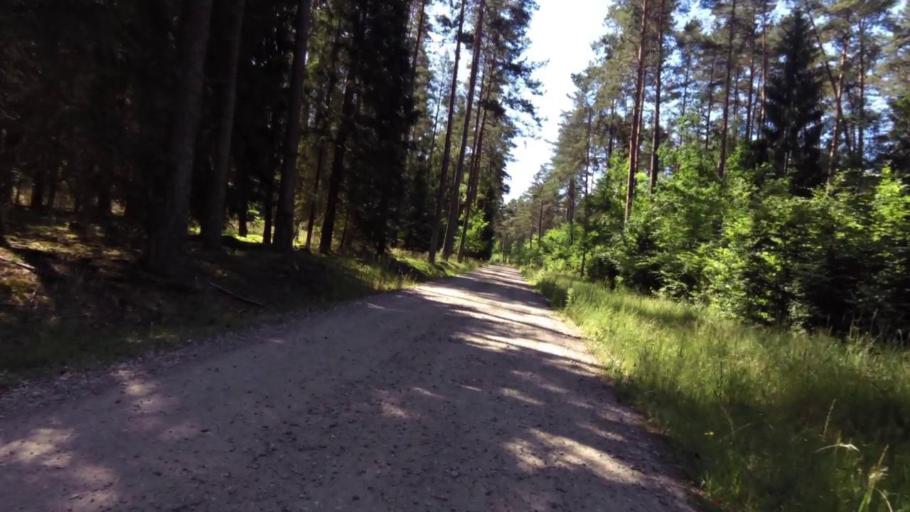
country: PL
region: West Pomeranian Voivodeship
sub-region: Powiat swidwinski
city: Rabino
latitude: 53.9138
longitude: 16.0064
